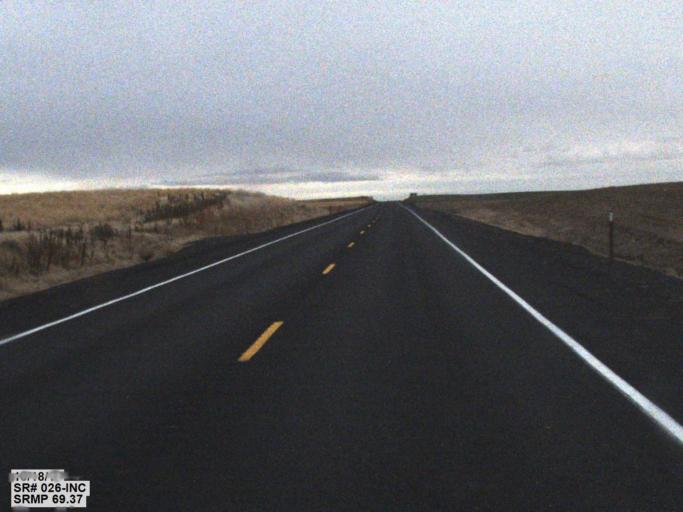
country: US
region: Washington
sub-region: Franklin County
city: Connell
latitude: 46.7947
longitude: -118.5731
